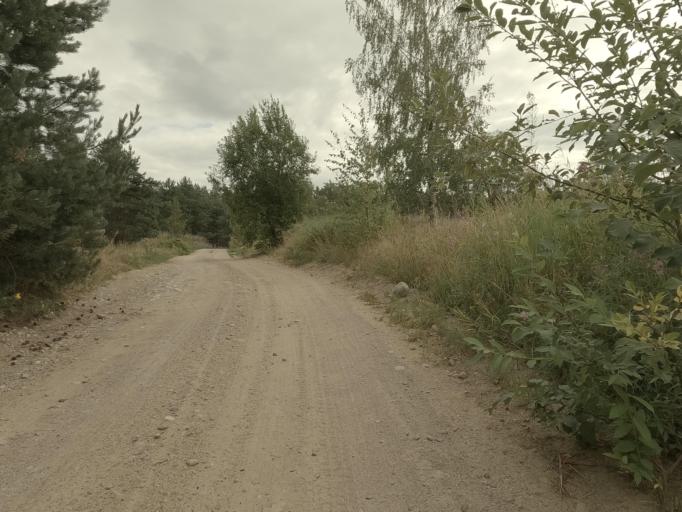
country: RU
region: Leningrad
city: Kamennogorsk
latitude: 60.9922
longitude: 29.1861
